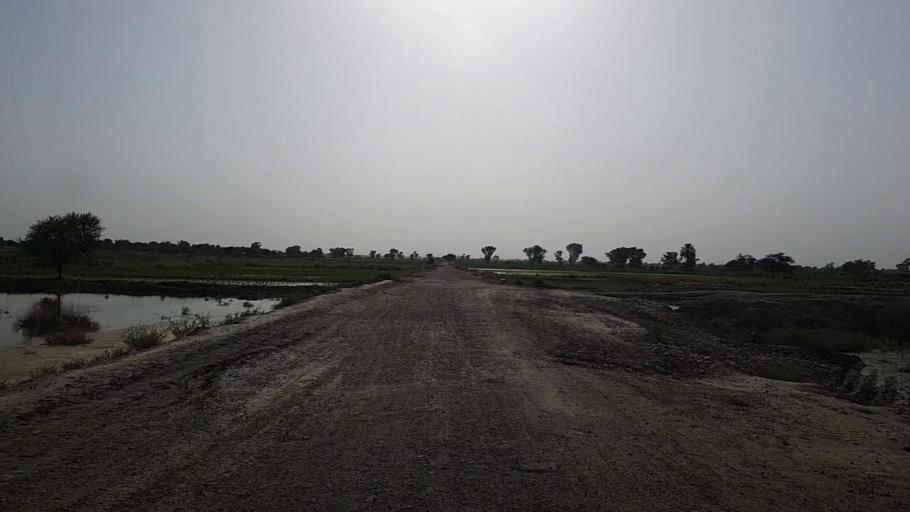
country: PK
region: Sindh
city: Pad Idan
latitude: 26.8532
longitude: 68.3100
